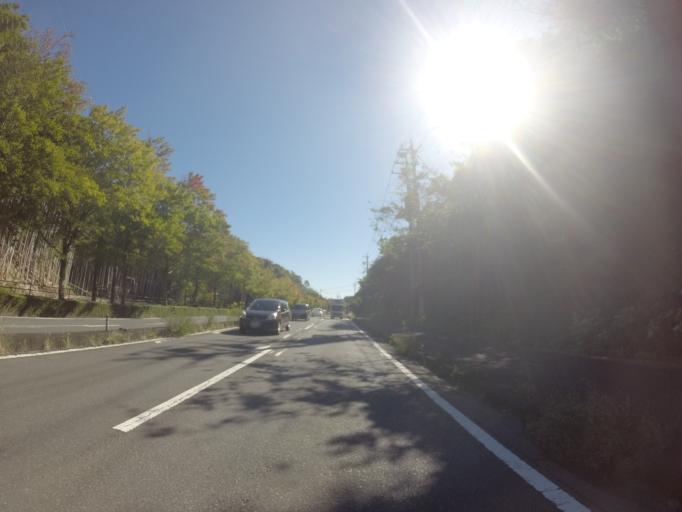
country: JP
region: Shizuoka
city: Fujieda
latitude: 34.8680
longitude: 138.2311
